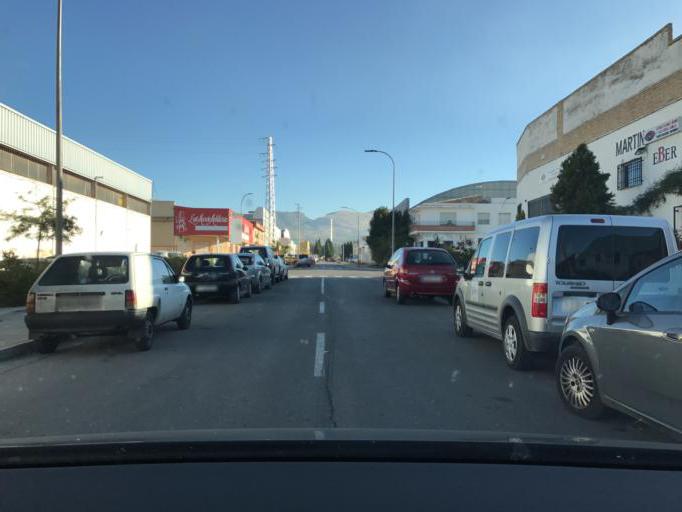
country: ES
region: Andalusia
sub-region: Provincia de Granada
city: Peligros
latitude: 37.2268
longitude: -3.6280
